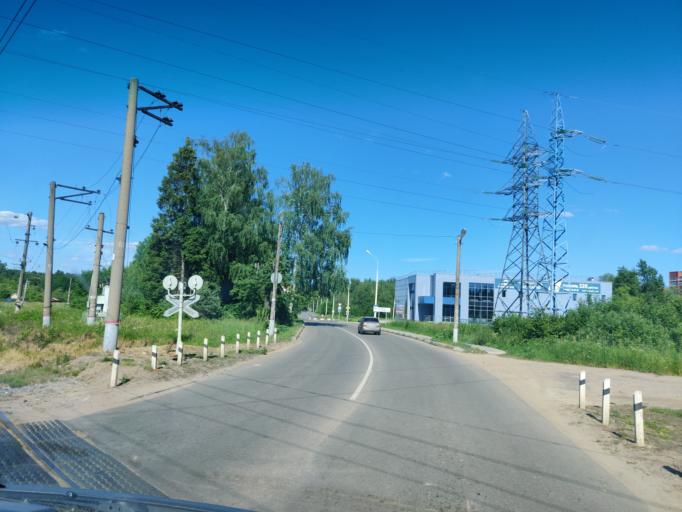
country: RU
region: Moskovskaya
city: Dubna
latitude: 56.7297
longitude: 37.1358
